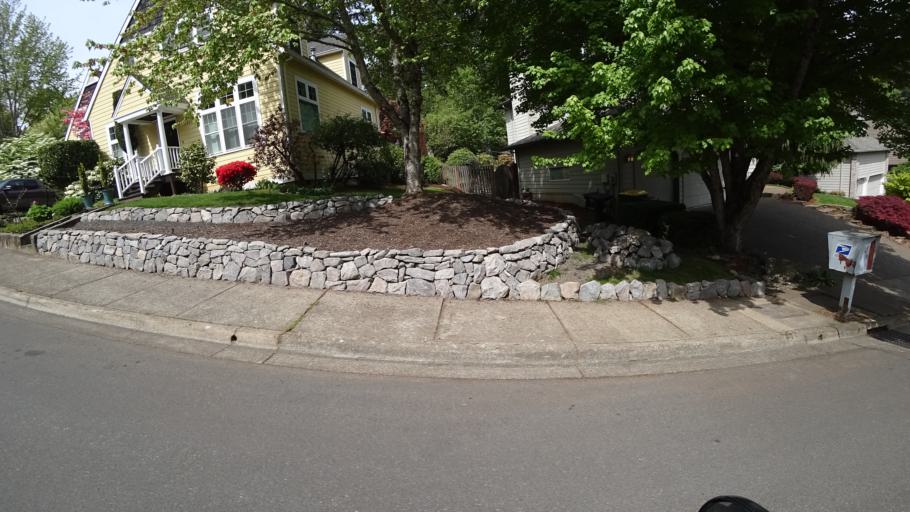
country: US
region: Oregon
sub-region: Washington County
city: Aloha
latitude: 45.4590
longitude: -122.8537
